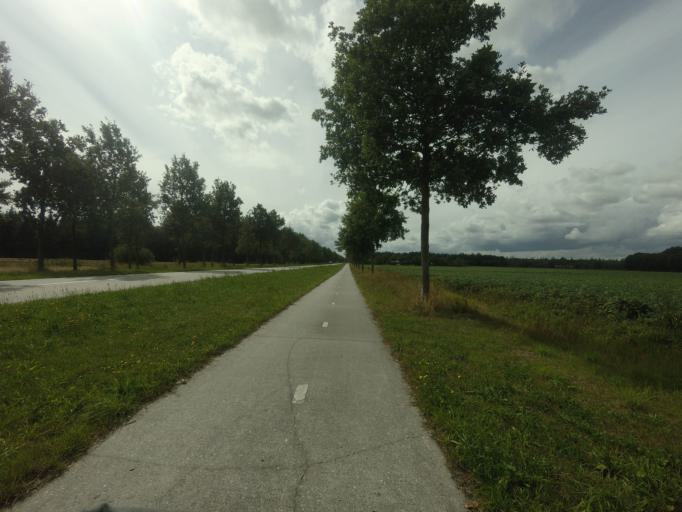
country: NL
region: Groningen
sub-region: Gemeente Leek
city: Leek
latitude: 53.0288
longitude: 6.4172
